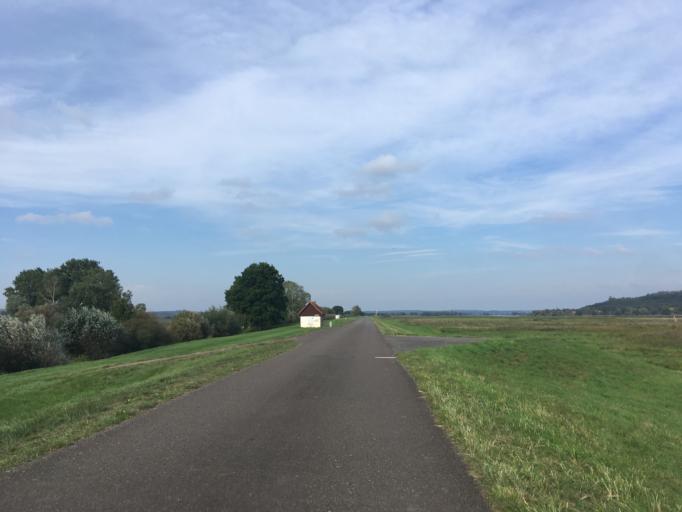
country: PL
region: West Pomeranian Voivodeship
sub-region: Powiat gryfinski
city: Cedynia
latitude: 52.9191
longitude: 14.1428
